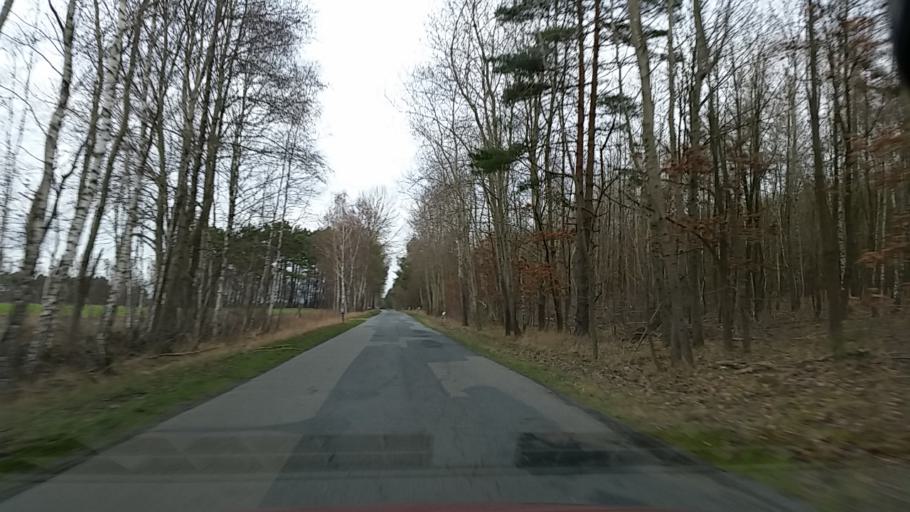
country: DE
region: Lower Saxony
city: Luder
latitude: 52.7867
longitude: 10.6693
